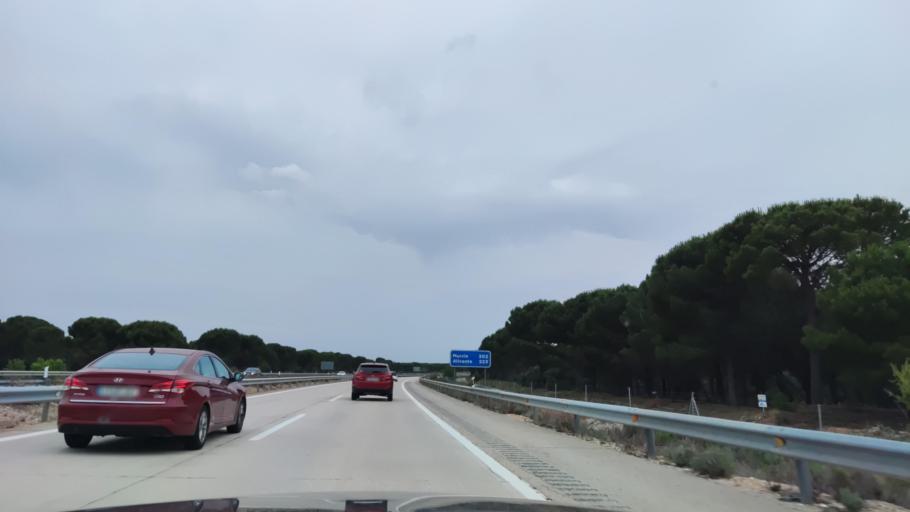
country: ES
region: Castille-La Mancha
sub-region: Provincia de Cuenca
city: Pozoamargo
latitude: 39.3500
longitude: -2.2014
